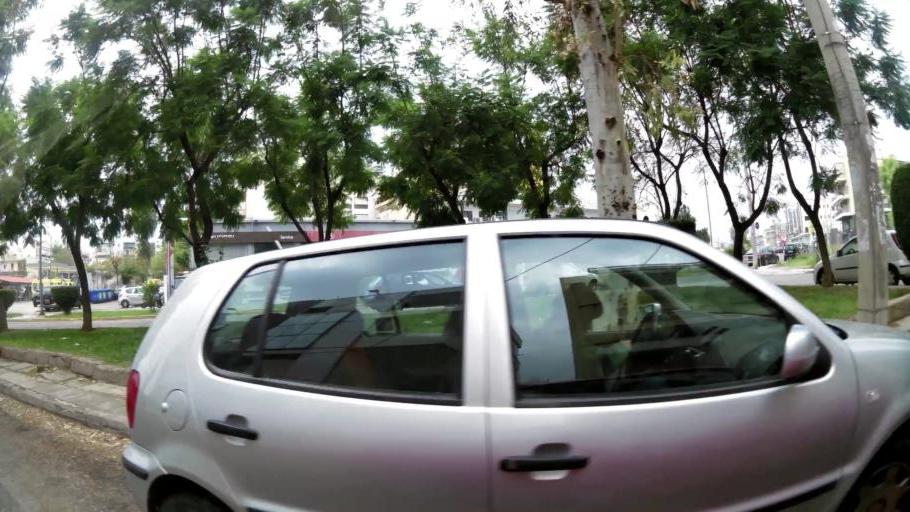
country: GR
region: Attica
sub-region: Nomarchia Athinas
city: Agioi Anargyroi
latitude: 38.0285
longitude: 23.7139
